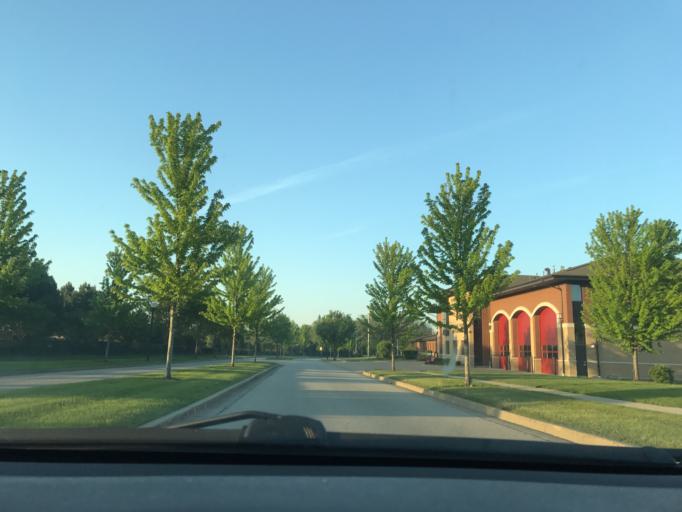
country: US
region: Illinois
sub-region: Kane County
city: South Elgin
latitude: 42.0098
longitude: -88.3595
